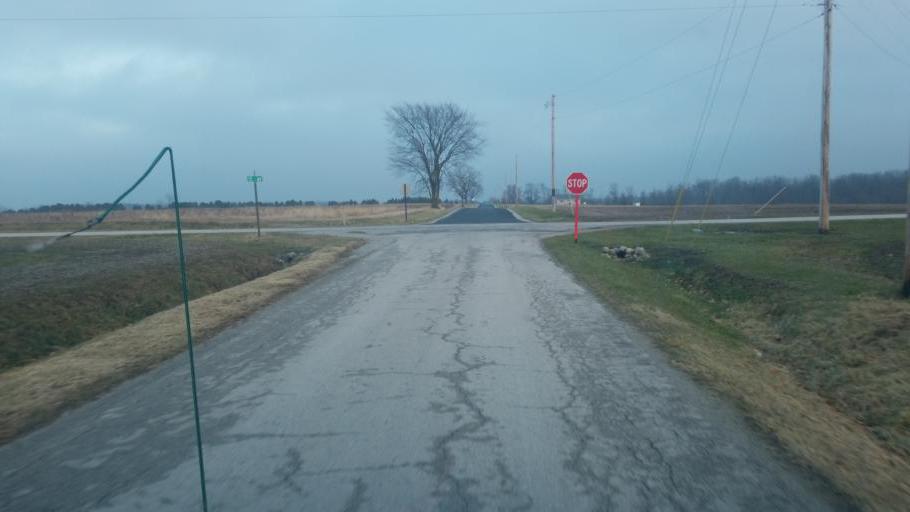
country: US
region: Ohio
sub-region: Wyandot County
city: Carey
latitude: 41.0072
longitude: -83.2623
